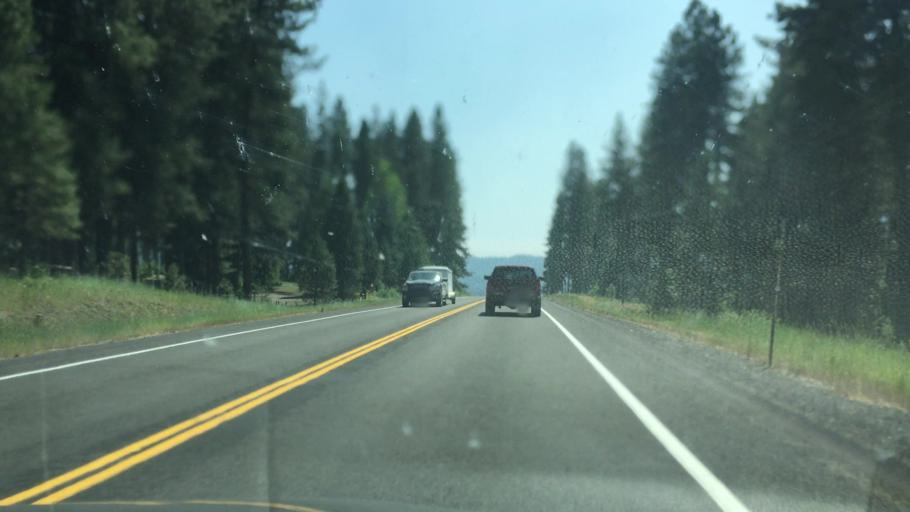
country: US
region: Idaho
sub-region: Valley County
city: McCall
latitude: 45.0952
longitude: -116.3076
